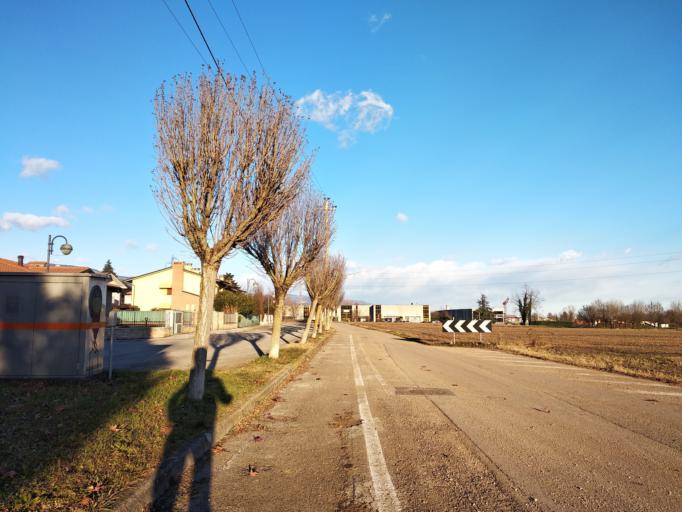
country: IT
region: Veneto
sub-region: Provincia di Vicenza
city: San Vito di Leguzzano
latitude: 45.6781
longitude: 11.3828
